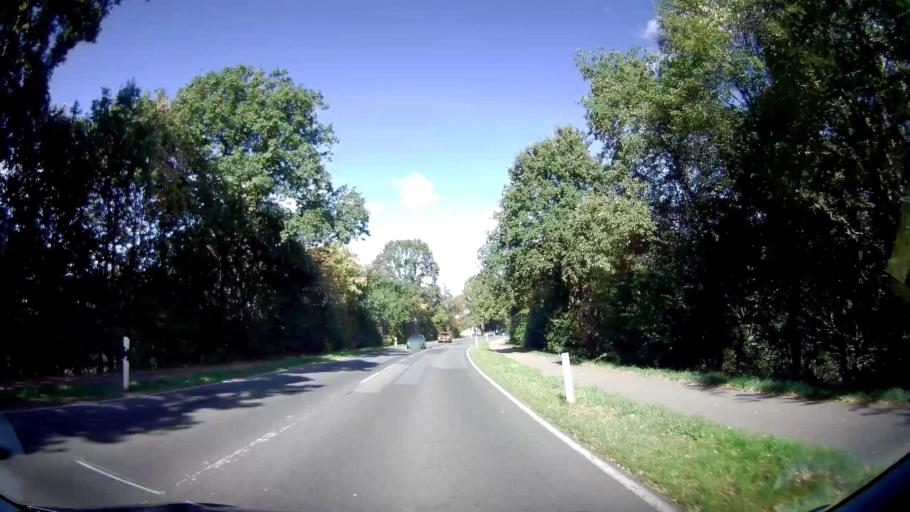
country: DE
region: North Rhine-Westphalia
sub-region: Regierungsbezirk Dusseldorf
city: Hunxe
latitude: 51.6401
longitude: 6.7590
